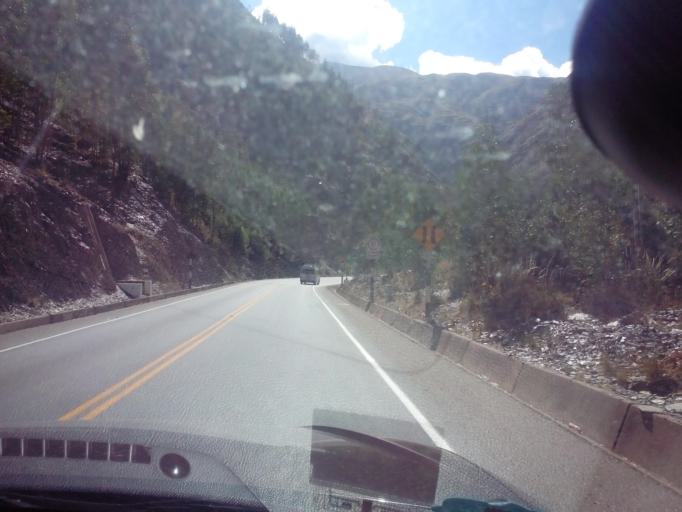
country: PE
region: Cusco
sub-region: Provincia de Quispicanchis
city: Urcos
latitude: -13.6877
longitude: -71.5957
